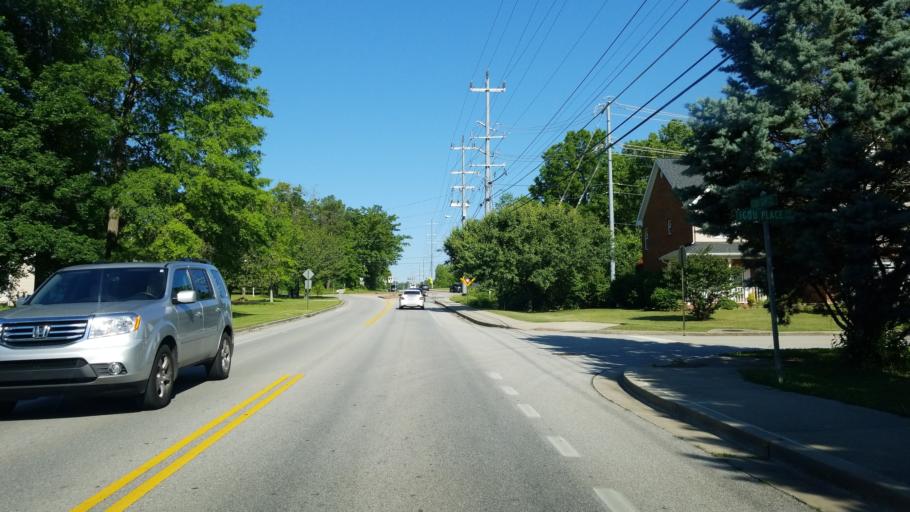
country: US
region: Tennessee
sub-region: Hamilton County
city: East Brainerd
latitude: 35.0245
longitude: -85.1510
